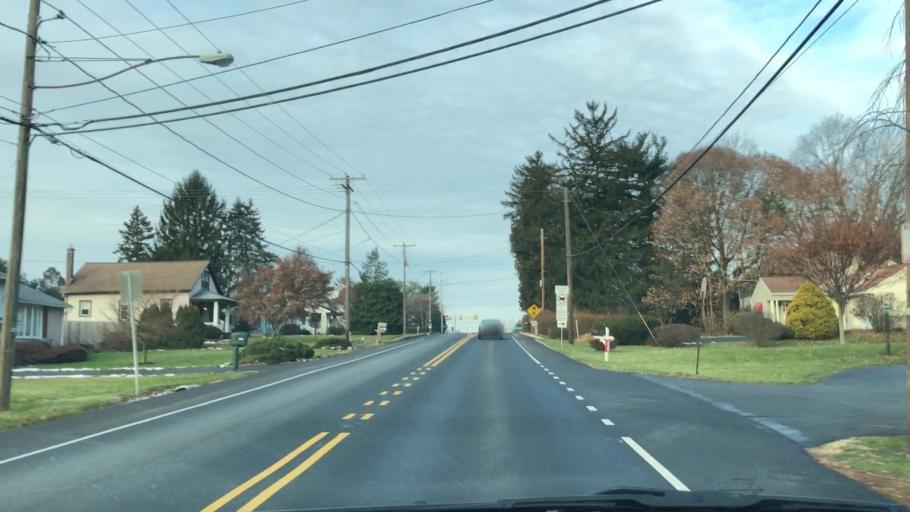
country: US
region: Pennsylvania
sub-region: Lancaster County
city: Mountville
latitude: 40.0572
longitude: -76.3959
